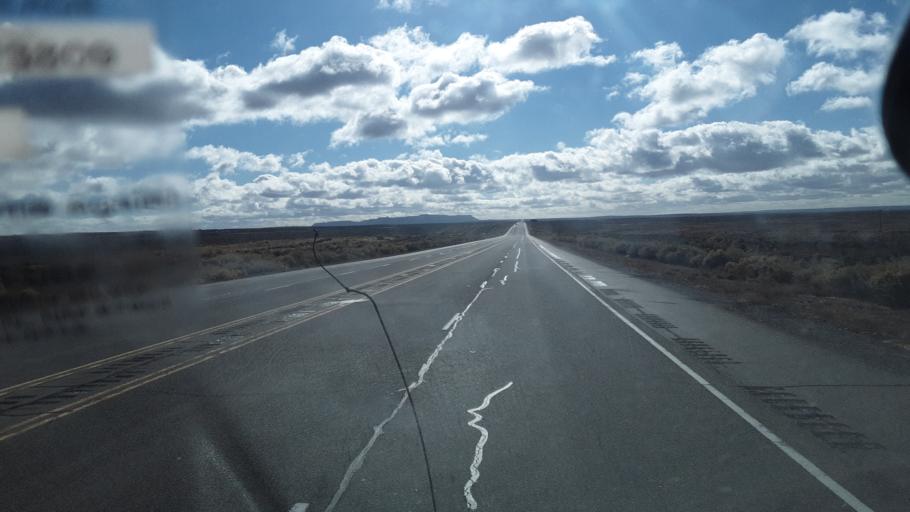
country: US
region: New Mexico
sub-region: San Juan County
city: Bloomfield
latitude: 36.5284
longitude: -107.9568
